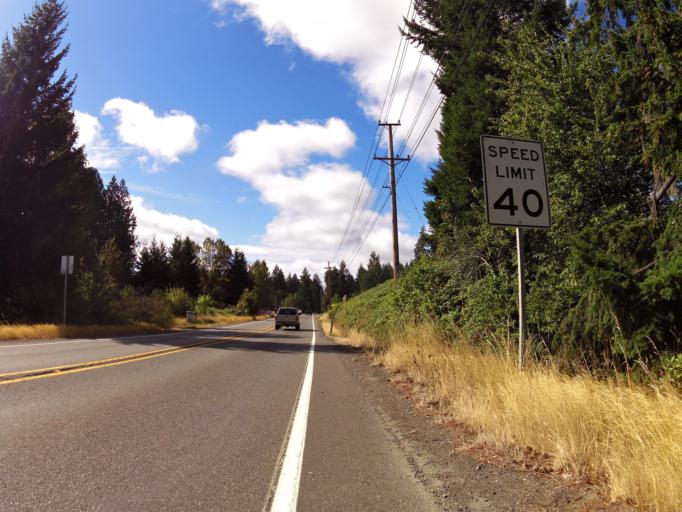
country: US
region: Washington
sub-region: Mason County
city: Shelton
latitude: 47.2513
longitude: -123.0419
